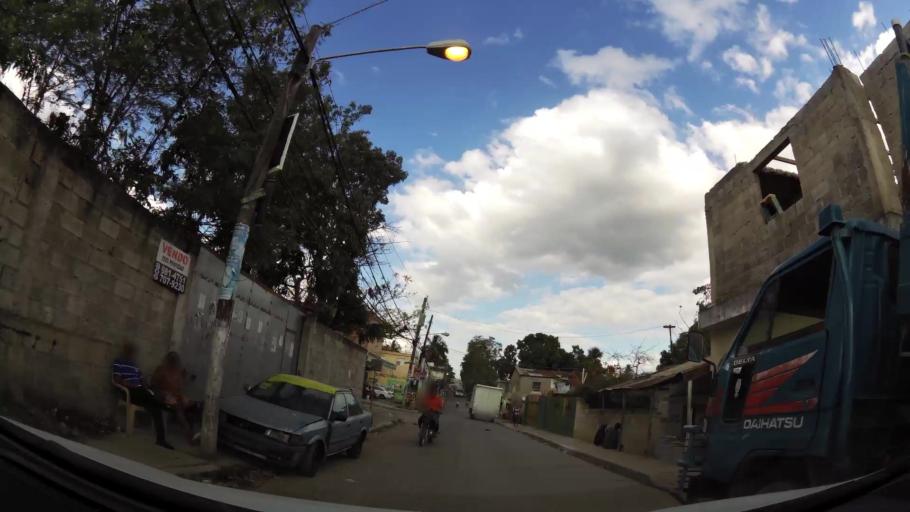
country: DO
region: Nacional
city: Ensanche Luperon
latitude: 18.5573
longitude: -69.9073
